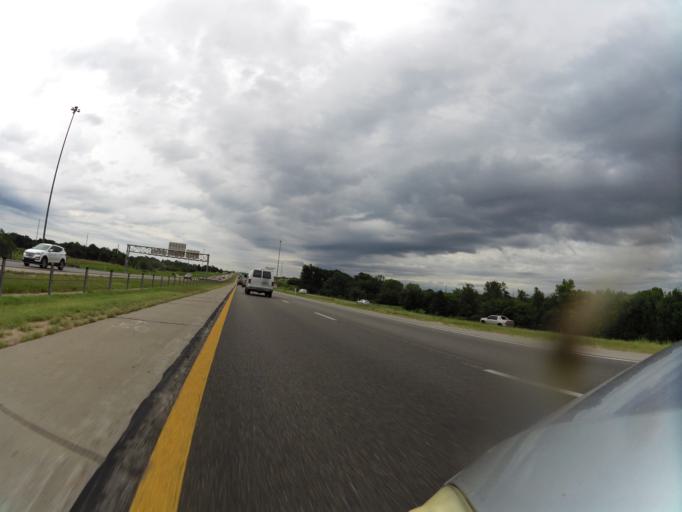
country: US
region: Kansas
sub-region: Sedgwick County
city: Bellaire
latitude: 37.7435
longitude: -97.3126
